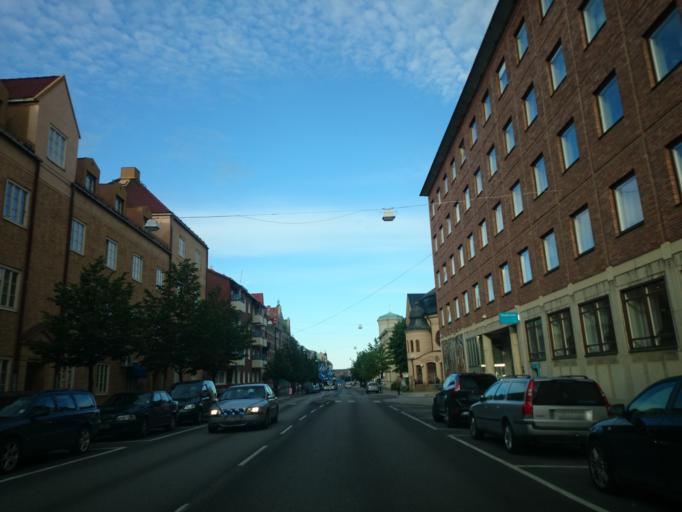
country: SE
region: Vaesternorrland
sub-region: Sundsvalls Kommun
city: Sundsvall
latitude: 62.3893
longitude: 17.3026
